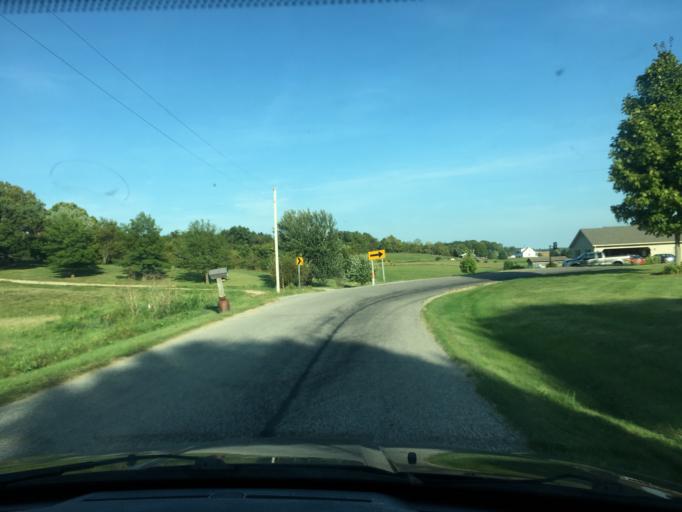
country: US
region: Ohio
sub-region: Logan County
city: West Liberty
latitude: 40.3017
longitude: -83.7462
